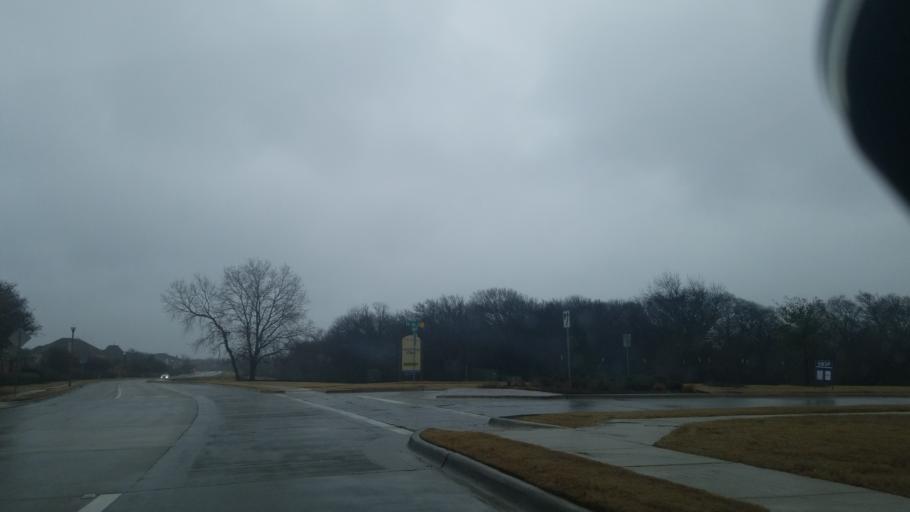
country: US
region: Texas
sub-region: Denton County
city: Corinth
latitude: 33.1723
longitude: -97.0630
